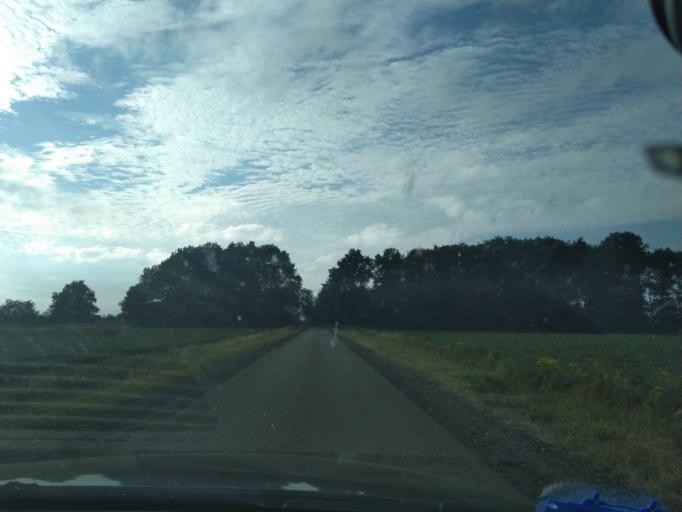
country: NL
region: Groningen
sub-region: Gemeente Vlagtwedde
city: Vlagtwedde
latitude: 53.0885
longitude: 7.1020
